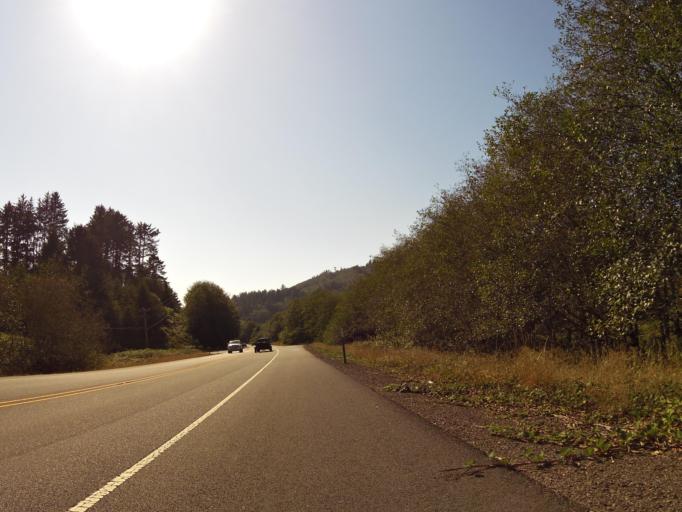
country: US
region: Oregon
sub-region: Tillamook County
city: Pacific City
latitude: 45.1577
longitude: -123.9509
